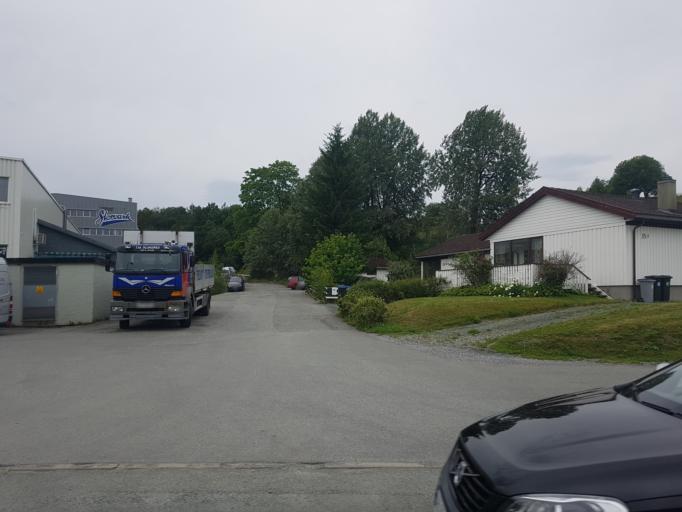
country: NO
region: Sor-Trondelag
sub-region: Trondheim
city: Trondheim
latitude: 63.3896
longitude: 10.3971
